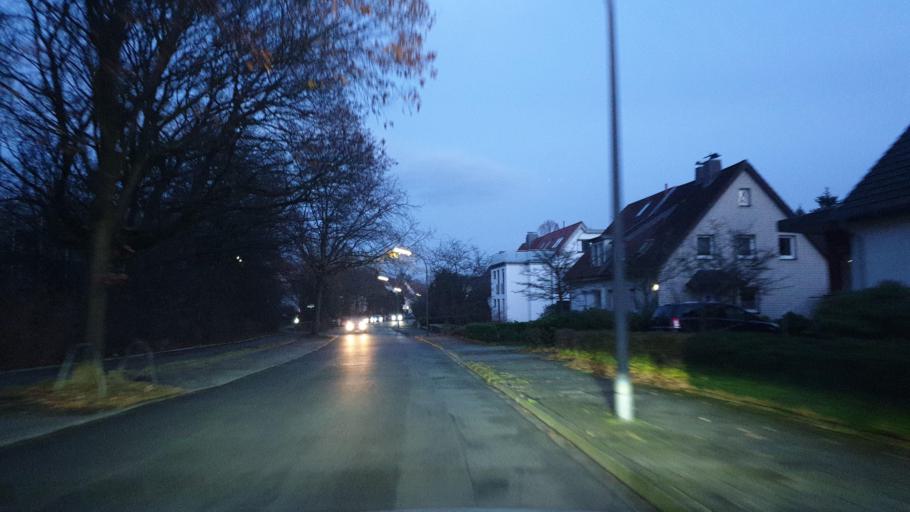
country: DE
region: Lower Saxony
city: Osnabrueck
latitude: 52.2692
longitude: 8.0122
